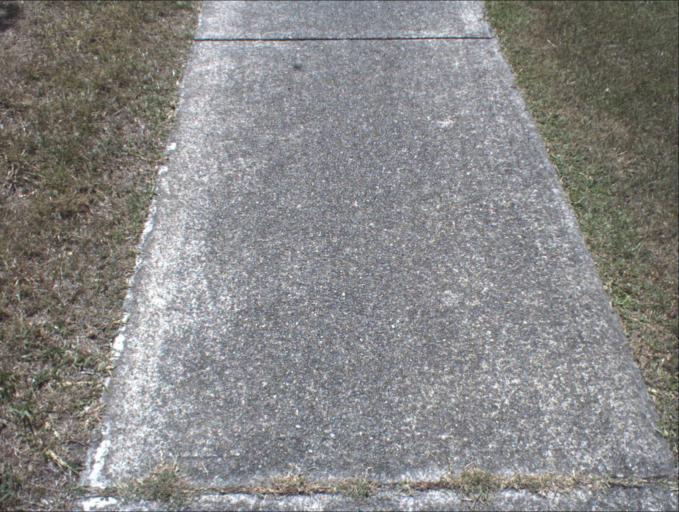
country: AU
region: Queensland
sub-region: Logan
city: Windaroo
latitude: -27.7288
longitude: 153.2043
